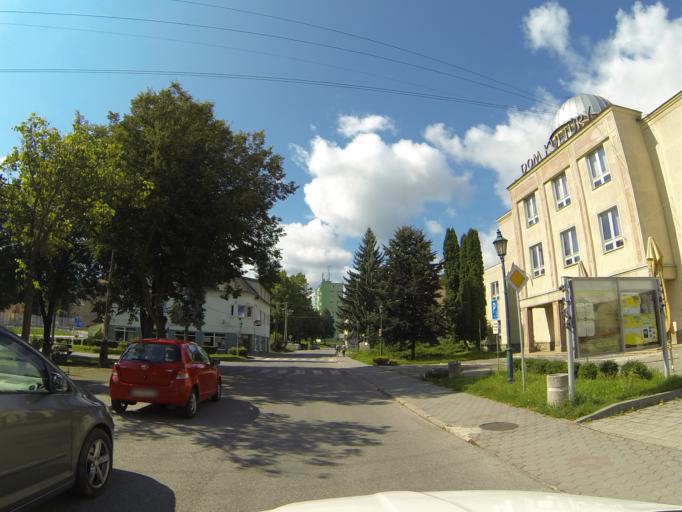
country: SK
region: Nitriansky
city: Handlova
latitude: 48.7273
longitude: 18.7594
